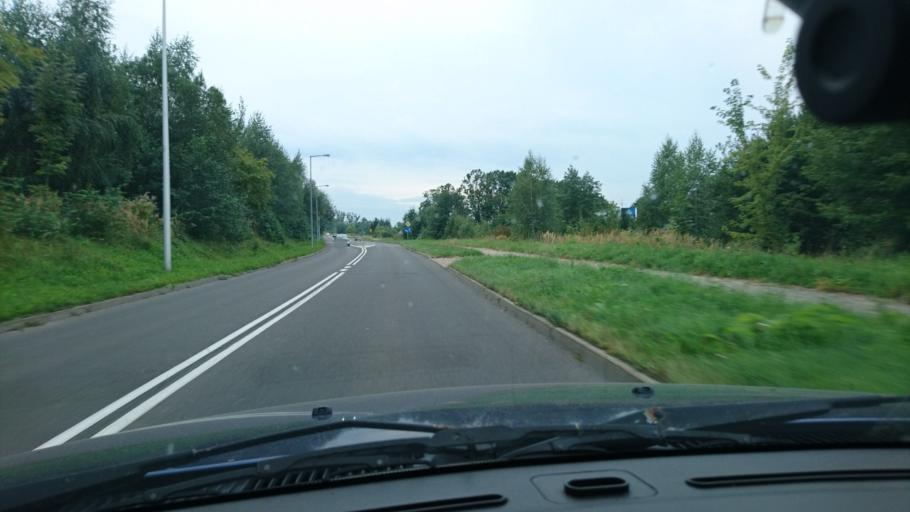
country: PL
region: Silesian Voivodeship
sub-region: Powiat bielski
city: Mazancowice
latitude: 49.8358
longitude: 19.0010
